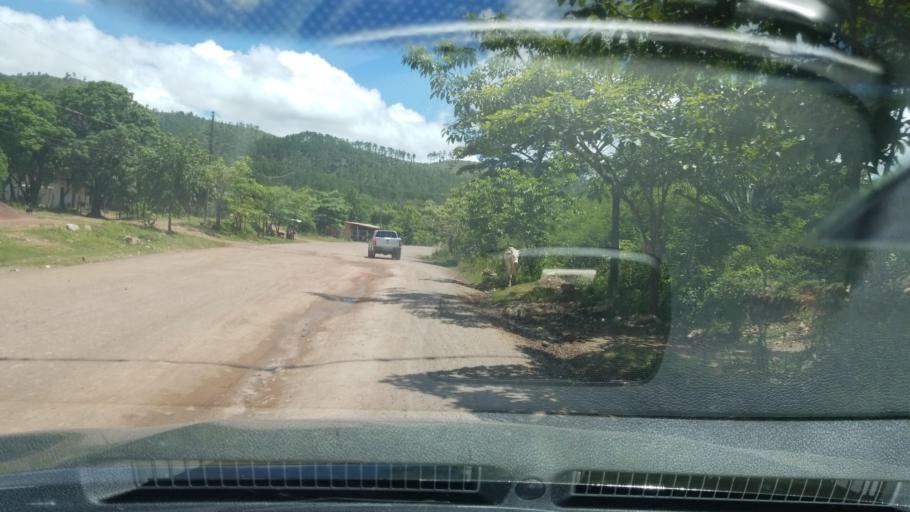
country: HN
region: Francisco Morazan
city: San Juan de Flores
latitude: 14.3351
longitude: -87.0469
